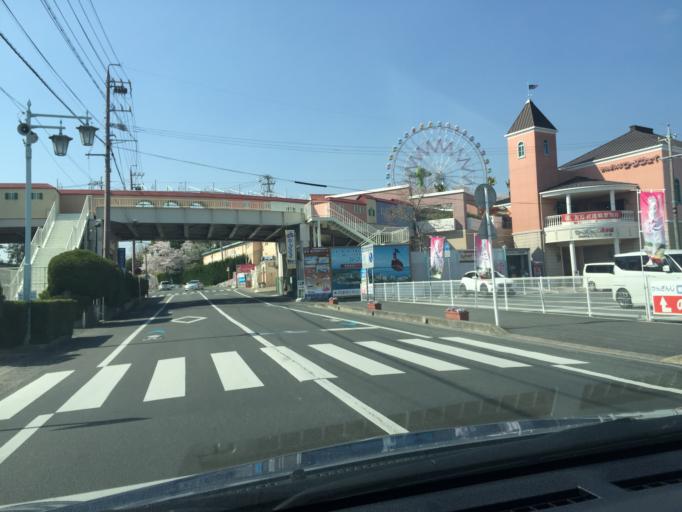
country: JP
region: Shizuoka
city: Kosai-shi
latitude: 34.7631
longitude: 137.6176
